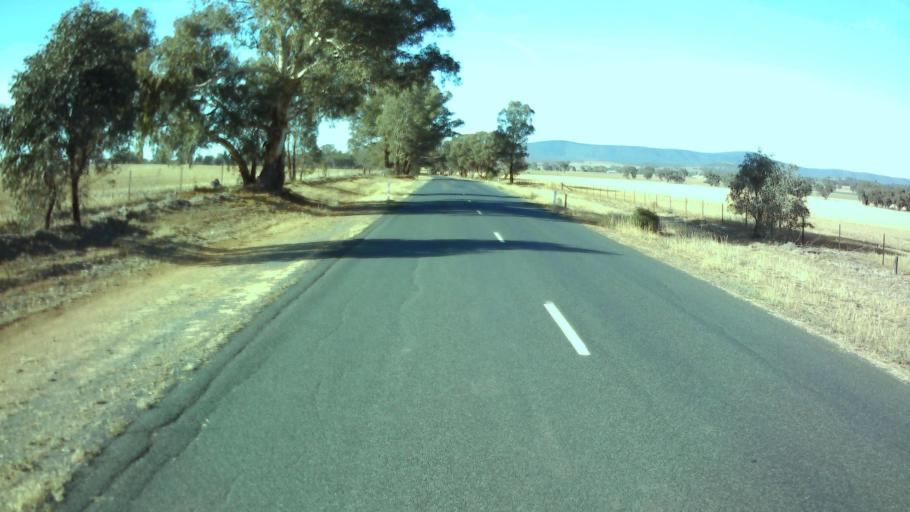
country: AU
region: New South Wales
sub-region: Weddin
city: Grenfell
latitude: -33.9207
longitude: 148.1404
